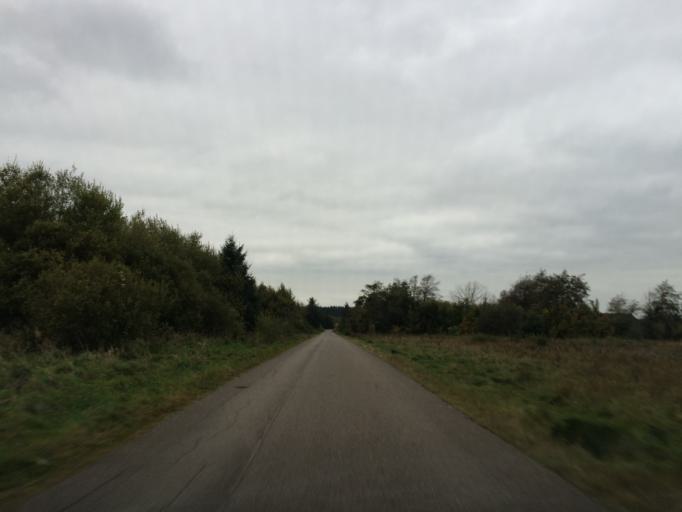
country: DK
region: Central Jutland
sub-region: Holstebro Kommune
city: Ulfborg
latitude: 56.2218
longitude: 8.4410
